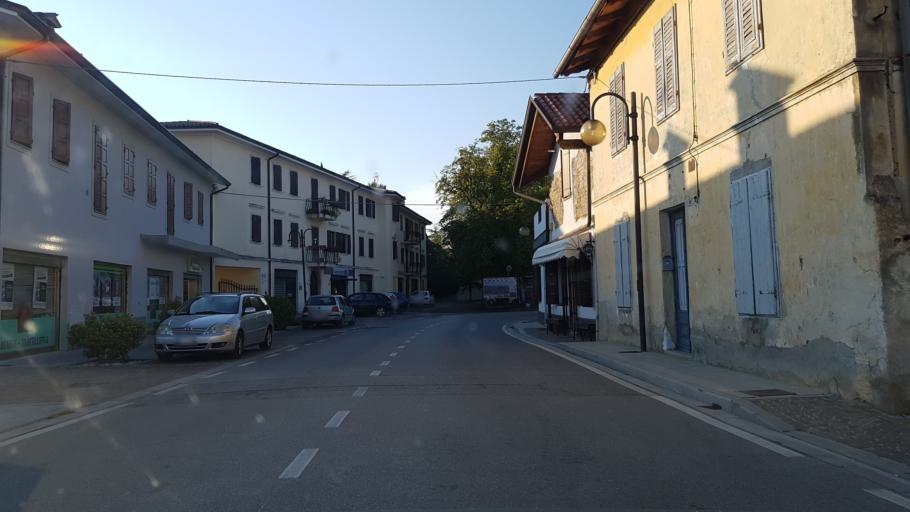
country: IT
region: Friuli Venezia Giulia
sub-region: Provincia di Gorizia
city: Capriva del Friuli
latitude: 45.9408
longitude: 13.5145
